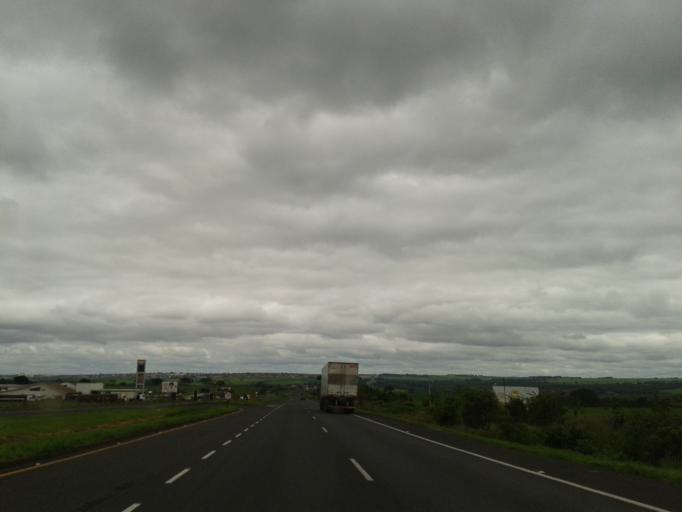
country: BR
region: Minas Gerais
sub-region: Uberlandia
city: Uberlandia
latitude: -19.0175
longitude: -48.2062
